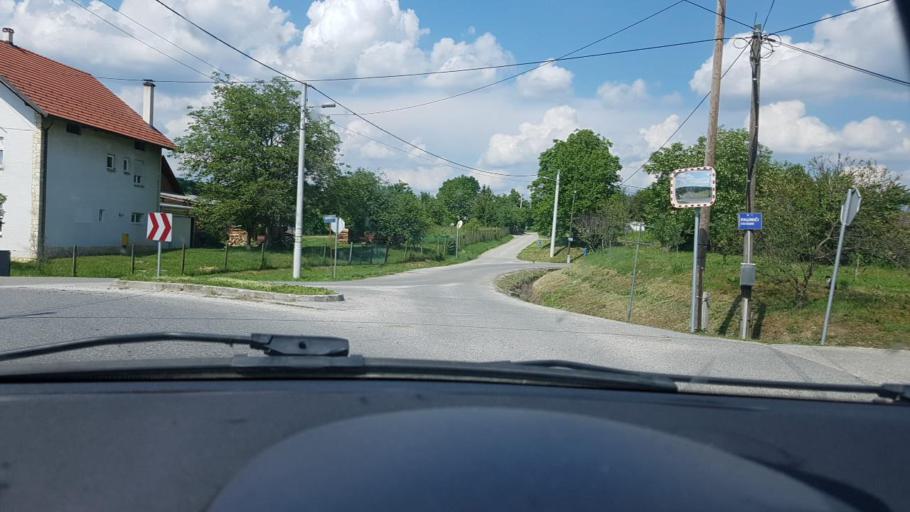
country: HR
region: Grad Zagreb
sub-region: Sesvete
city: Sesvete
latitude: 45.8865
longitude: 16.1749
